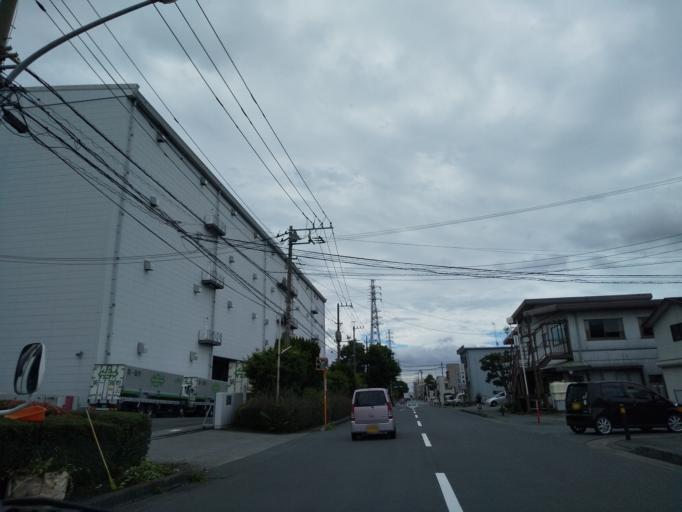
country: JP
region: Kanagawa
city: Zama
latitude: 35.5174
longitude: 139.3397
